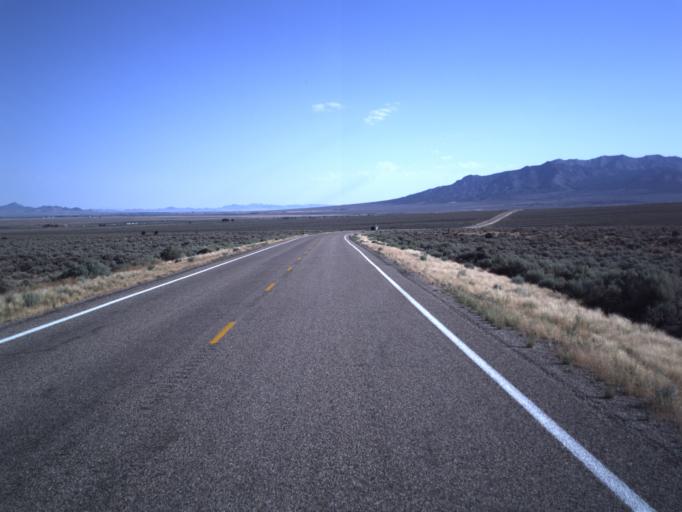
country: US
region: Utah
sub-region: Beaver County
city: Milford
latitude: 38.1476
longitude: -112.9598
